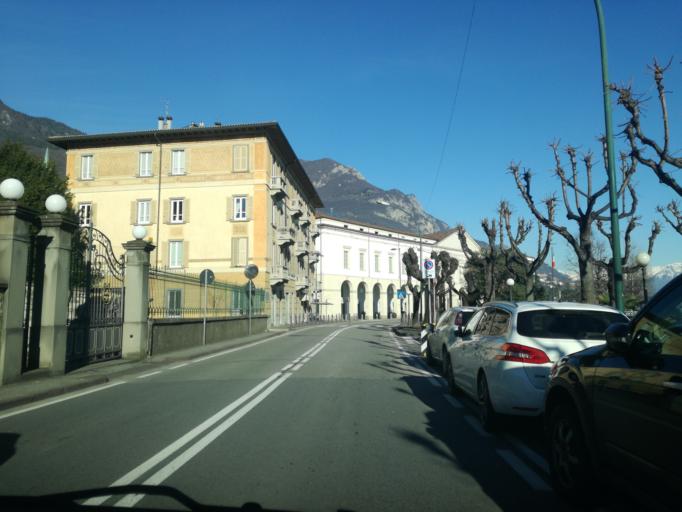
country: IT
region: Lombardy
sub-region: Provincia di Bergamo
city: Lovere
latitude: 45.8137
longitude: 10.0722
